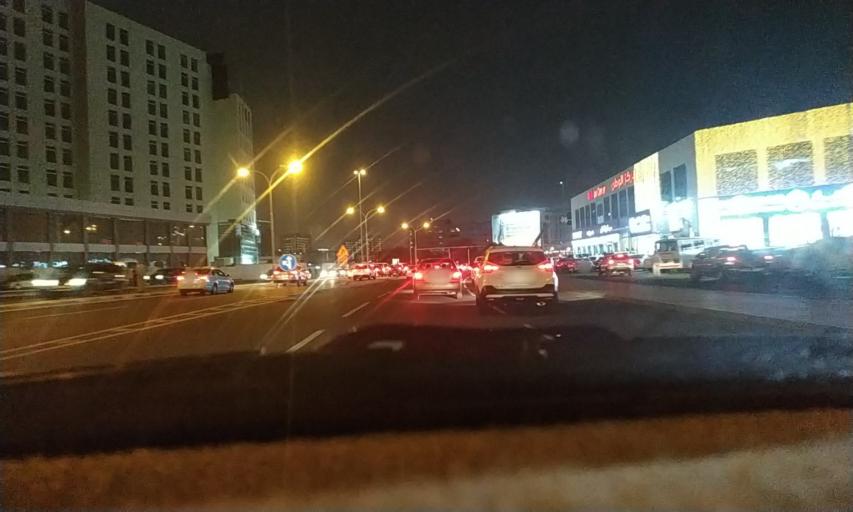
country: QA
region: Baladiyat ad Dawhah
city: Doha
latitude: 25.2784
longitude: 51.5364
